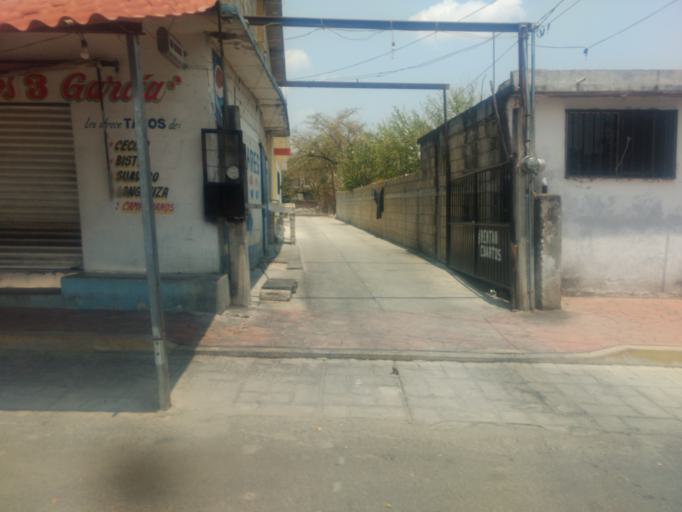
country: MX
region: Morelos
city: La Joya
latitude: 18.7018
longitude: -99.4805
